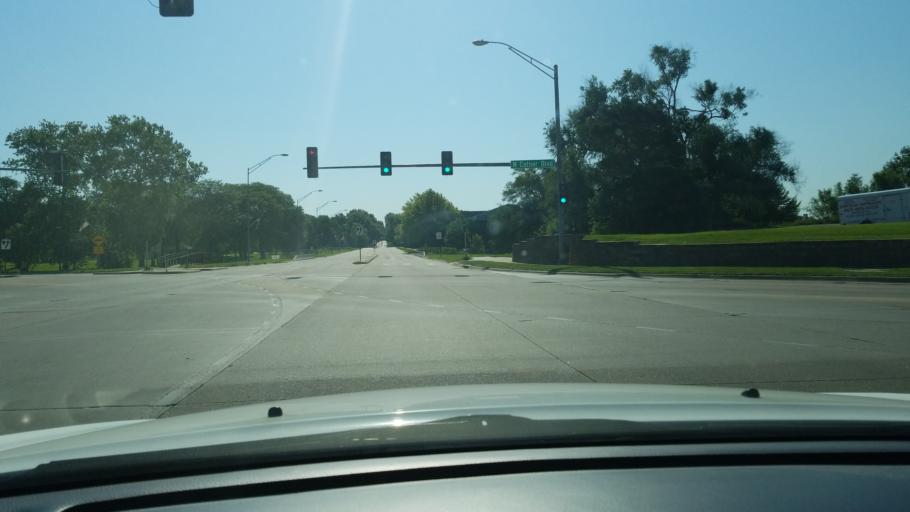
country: US
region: Nebraska
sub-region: Lancaster County
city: Lincoln
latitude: 40.8206
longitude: -96.6356
